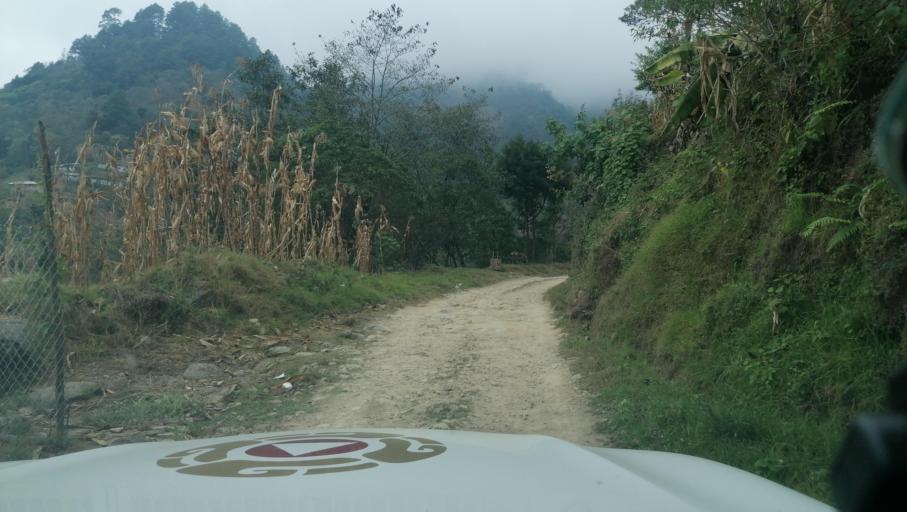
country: GT
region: San Marcos
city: Tacana
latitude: 15.2079
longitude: -92.1706
